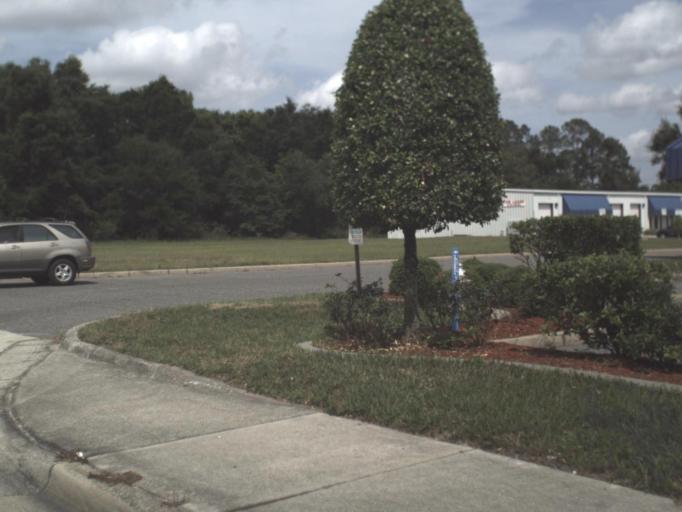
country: US
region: Florida
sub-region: Clay County
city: Lakeside
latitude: 30.1346
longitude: -81.7795
